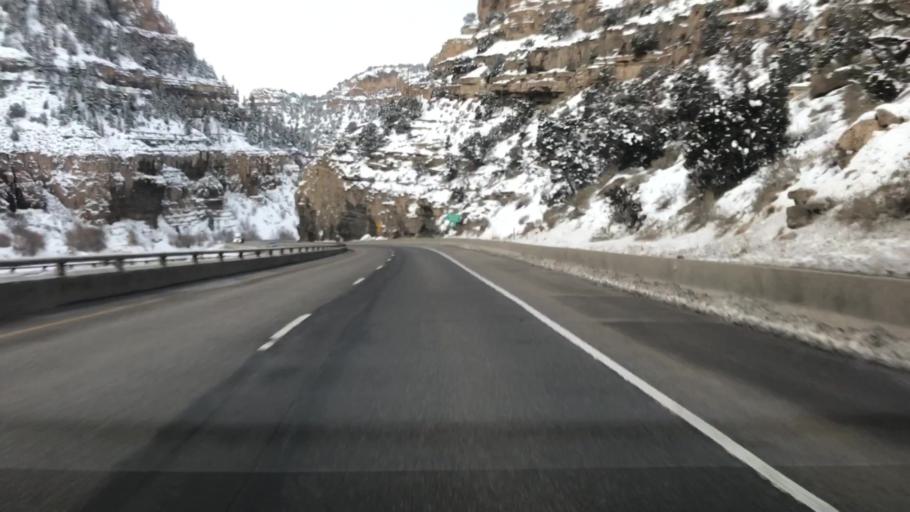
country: US
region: Colorado
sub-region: Eagle County
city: Gypsum
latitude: 39.6254
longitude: -107.1123
